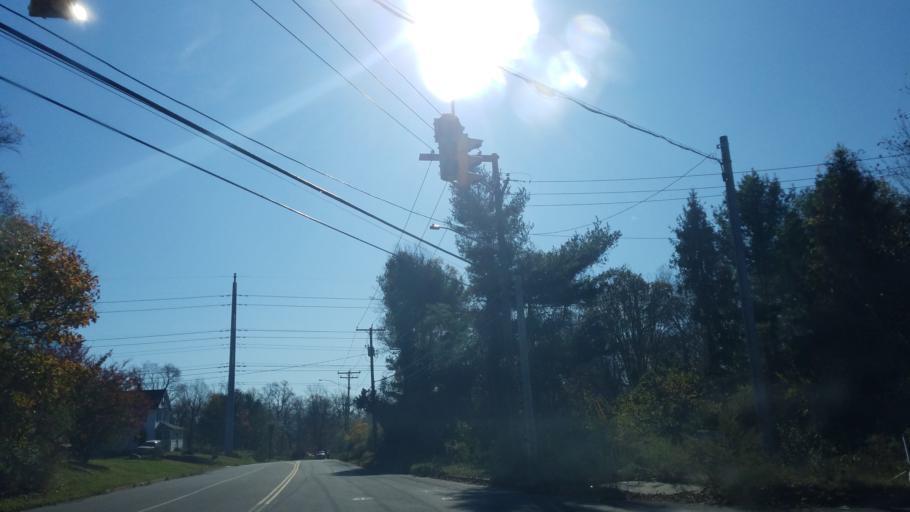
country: US
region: Connecticut
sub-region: New Haven County
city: City of Milford (balance)
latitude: 41.2453
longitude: -73.0748
